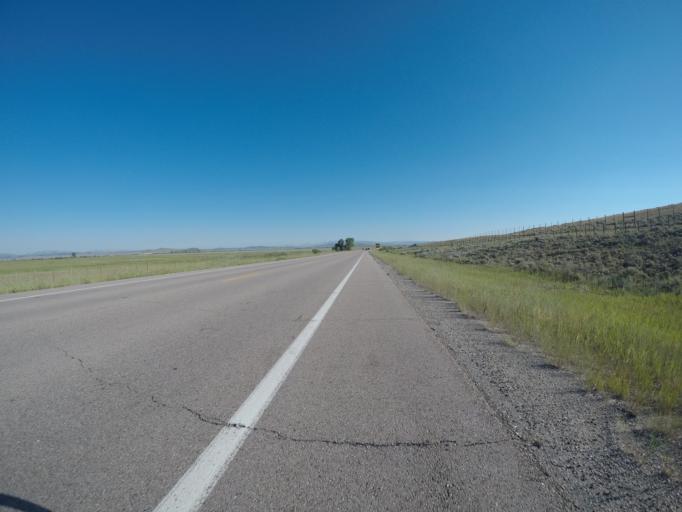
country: US
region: Wyoming
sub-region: Sublette County
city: Pinedale
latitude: 42.9498
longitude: -110.0856
